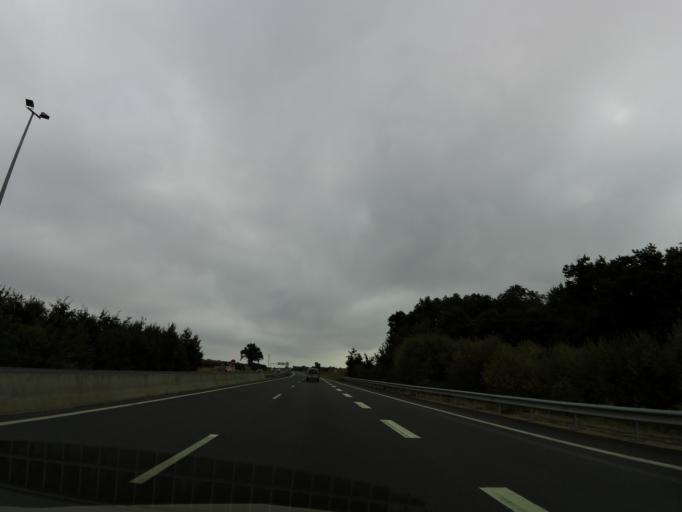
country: FR
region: Pays de la Loire
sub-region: Departement de la Vendee
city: La Ferriere
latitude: 46.6738
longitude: -1.3434
